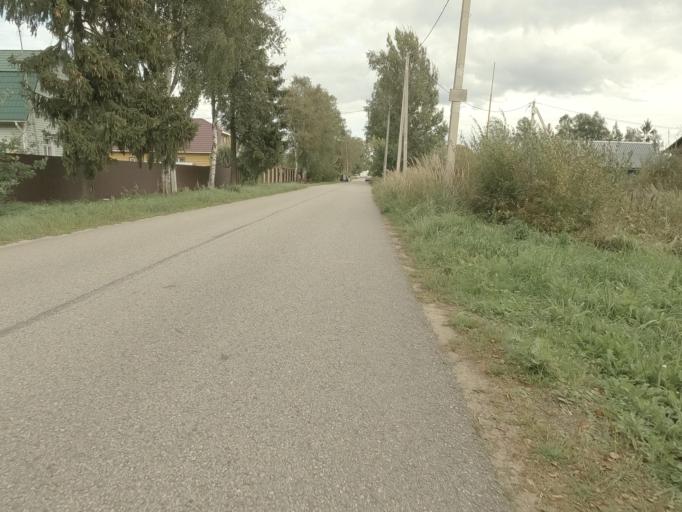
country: RU
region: Leningrad
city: Mga
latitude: 59.7602
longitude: 31.0311
